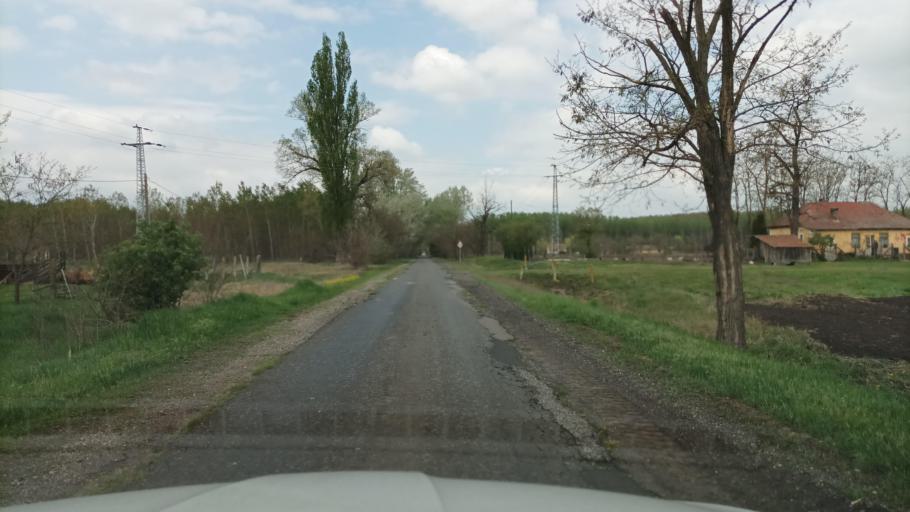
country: HU
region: Pest
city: Kocser
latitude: 47.0445
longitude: 19.9307
